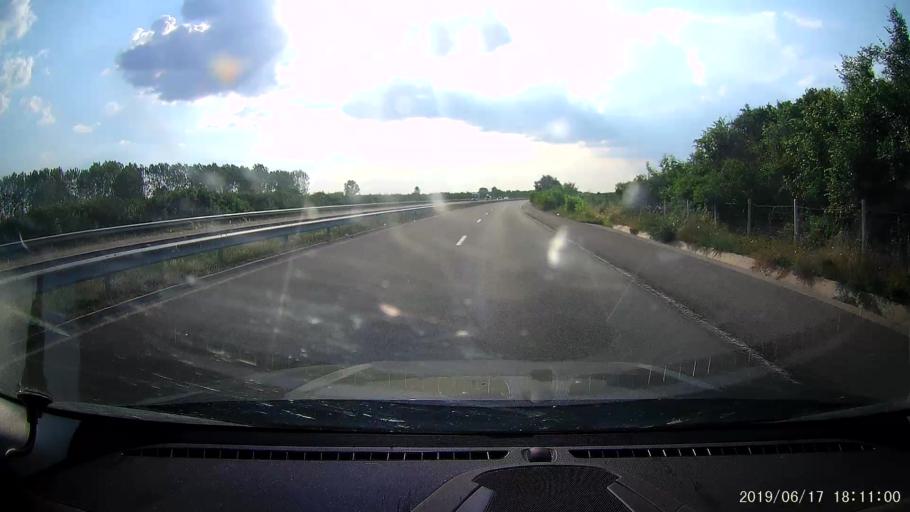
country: BG
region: Khaskovo
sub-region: Obshtina Lyubimets
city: Lyubimets
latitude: 41.8782
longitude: 26.0619
